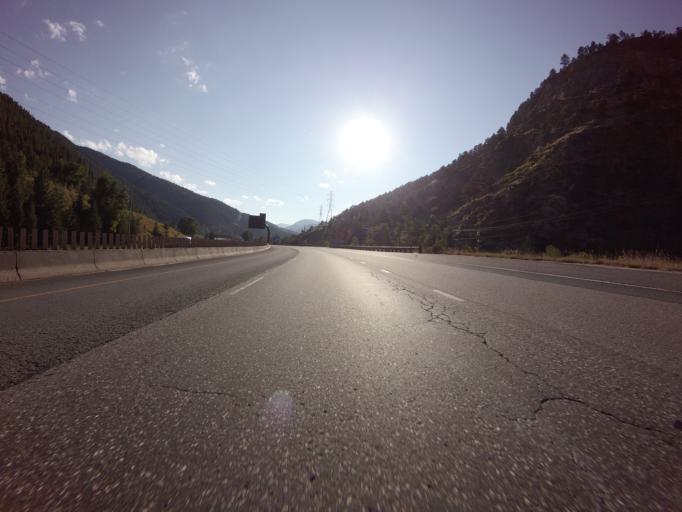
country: US
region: Colorado
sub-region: Clear Creek County
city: Idaho Springs
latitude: 39.7447
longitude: -105.4883
